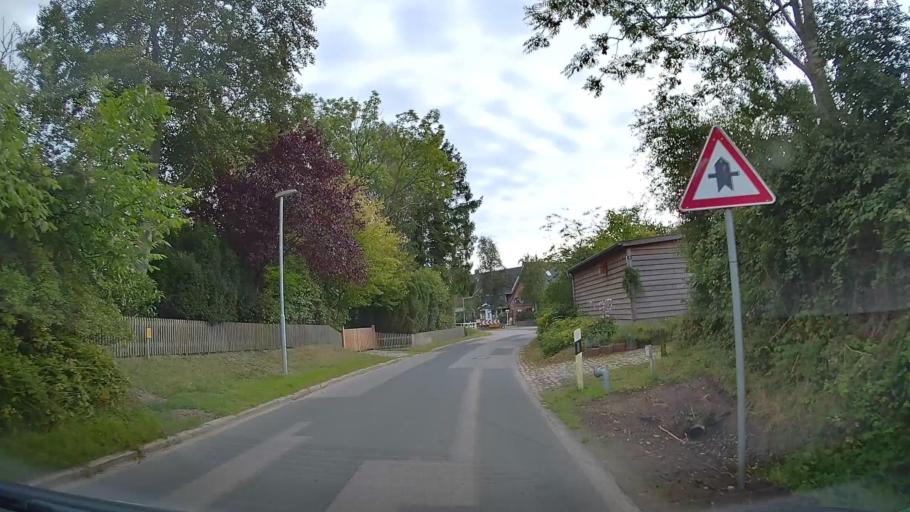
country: DE
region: Schleswig-Holstein
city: Panker
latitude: 54.3491
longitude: 10.5789
